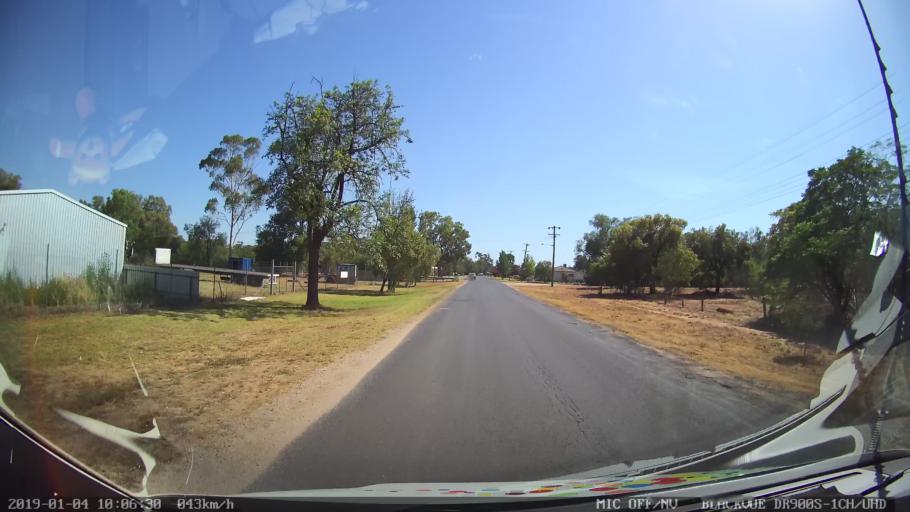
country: AU
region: New South Wales
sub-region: Cabonne
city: Canowindra
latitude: -33.4334
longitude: 148.3688
